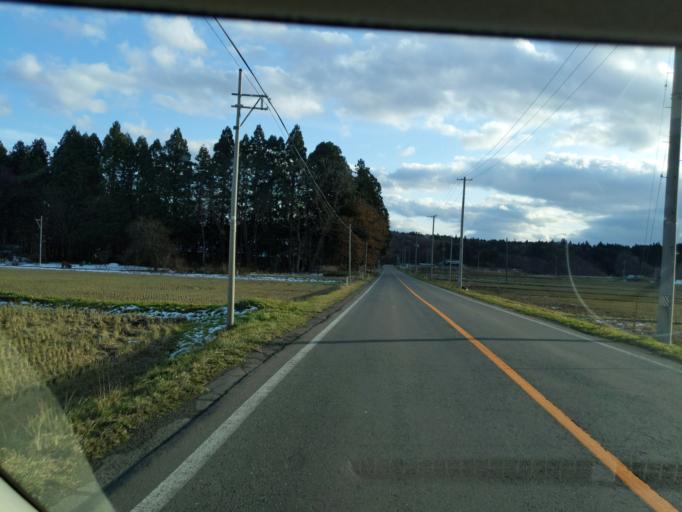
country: JP
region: Iwate
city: Mizusawa
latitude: 39.1905
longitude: 141.0525
